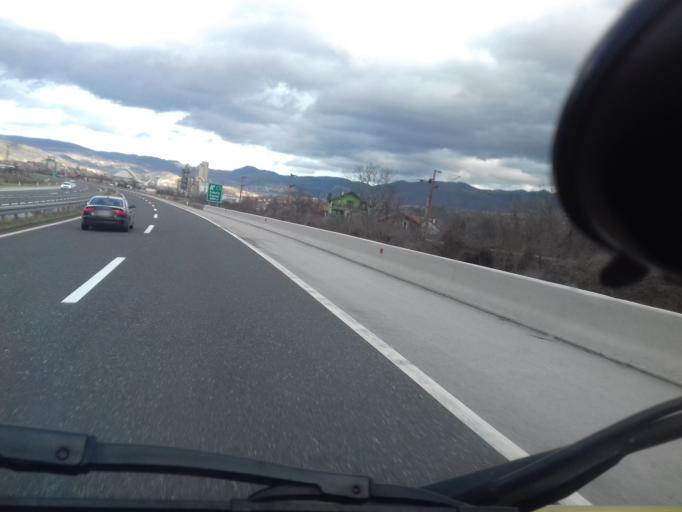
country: BA
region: Federation of Bosnia and Herzegovina
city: Kakanj
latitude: 44.1059
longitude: 18.1112
